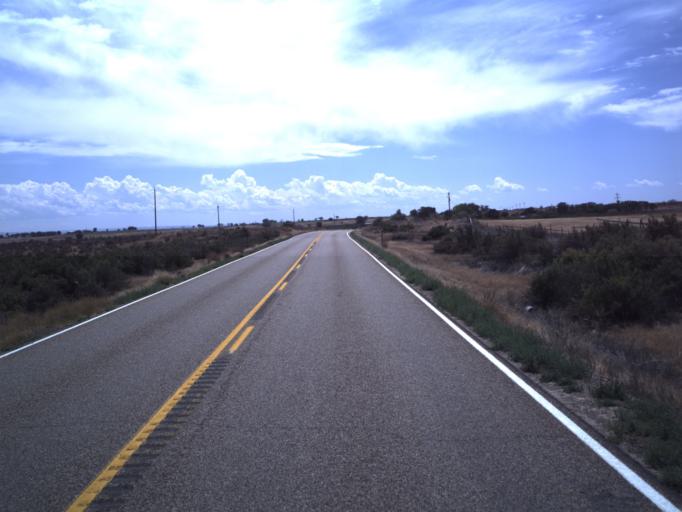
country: US
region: Utah
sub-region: Uintah County
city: Maeser
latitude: 40.2611
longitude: -109.6849
